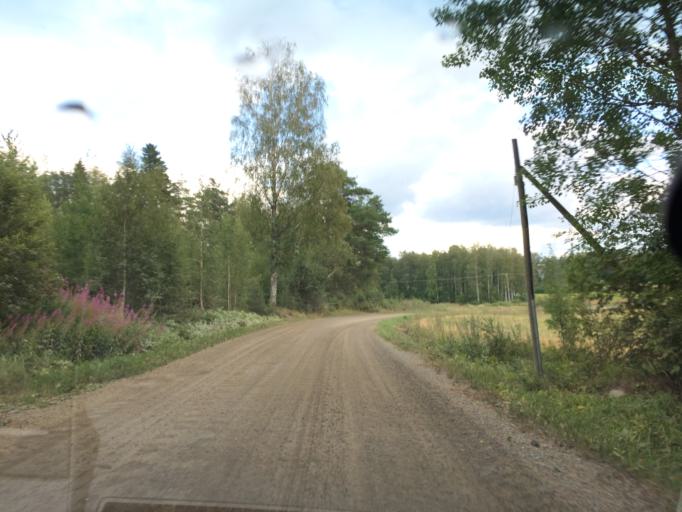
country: FI
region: Pirkanmaa
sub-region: Tampere
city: Luopioinen
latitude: 61.2648
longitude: 24.6974
